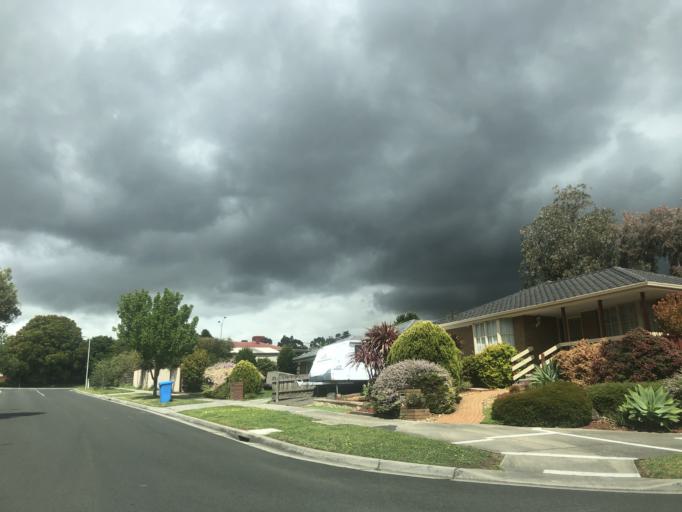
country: AU
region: Victoria
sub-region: Casey
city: Endeavour Hills
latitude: -37.9718
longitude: 145.2599
